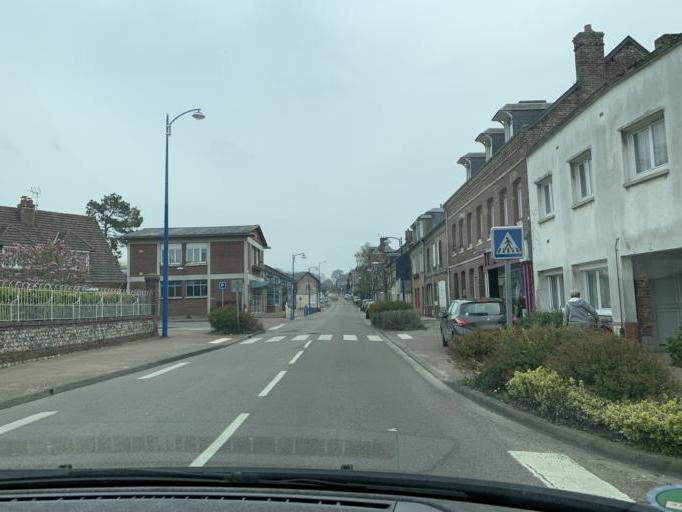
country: FR
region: Haute-Normandie
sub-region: Departement de la Seine-Maritime
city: Saint-Valery-en-Caux
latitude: 49.8623
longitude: 0.7142
